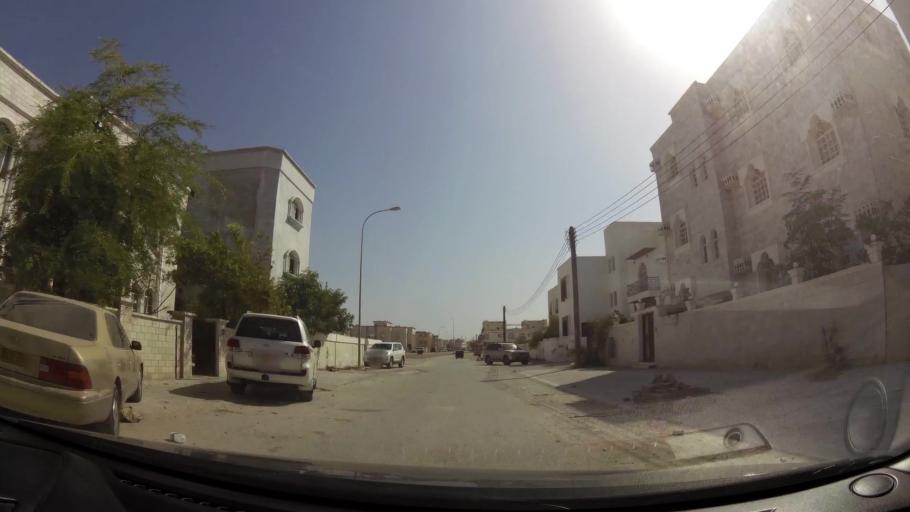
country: OM
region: Zufar
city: Salalah
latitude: 17.0037
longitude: 54.0138
